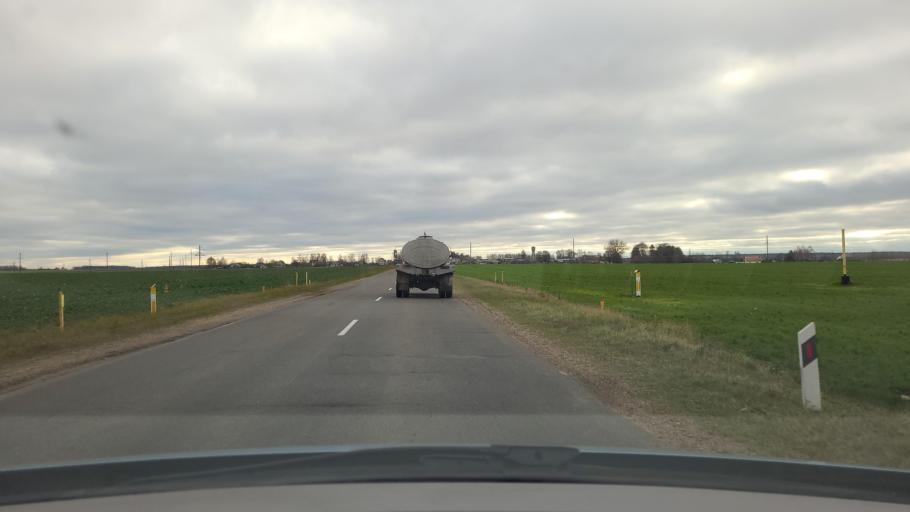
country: BY
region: Minsk
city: Krupki
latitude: 54.3767
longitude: 29.0533
